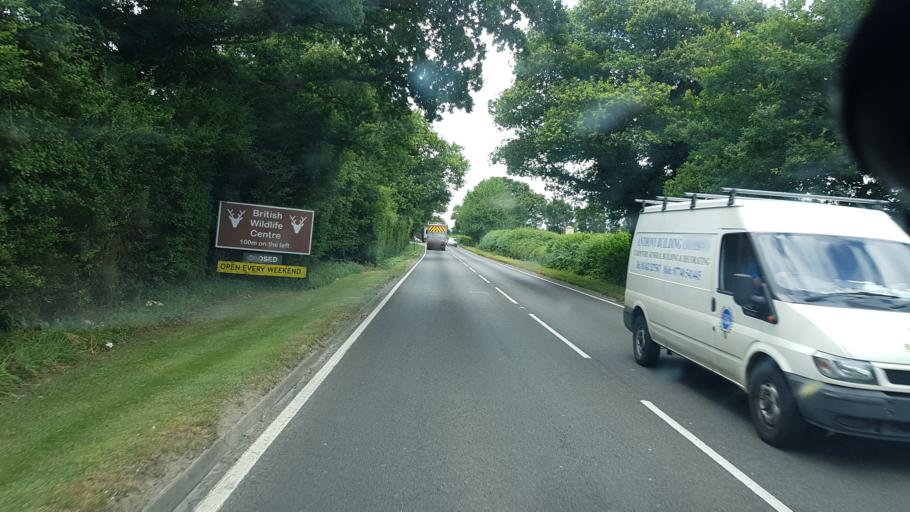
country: GB
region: England
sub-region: Surrey
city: Lingfield
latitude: 51.1752
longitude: -0.0492
